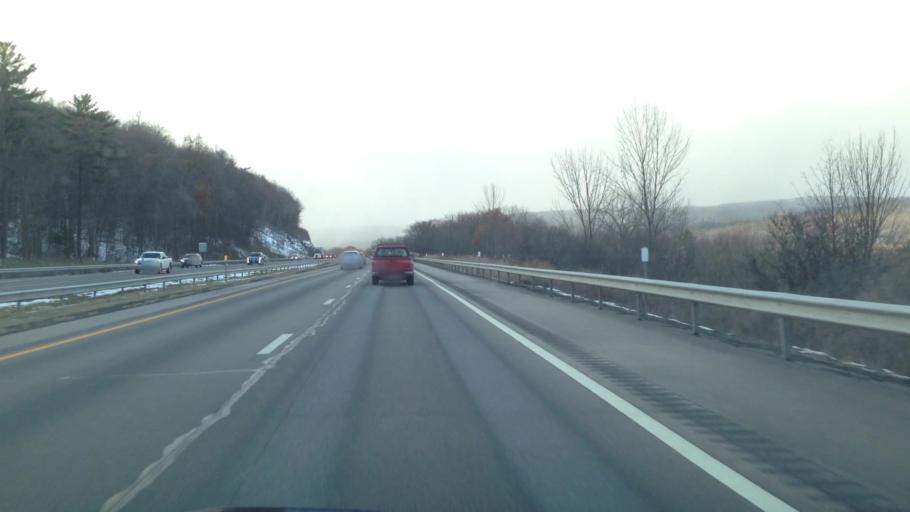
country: US
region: New York
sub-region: Schenectady County
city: Scotia
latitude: 42.8587
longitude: -74.0350
